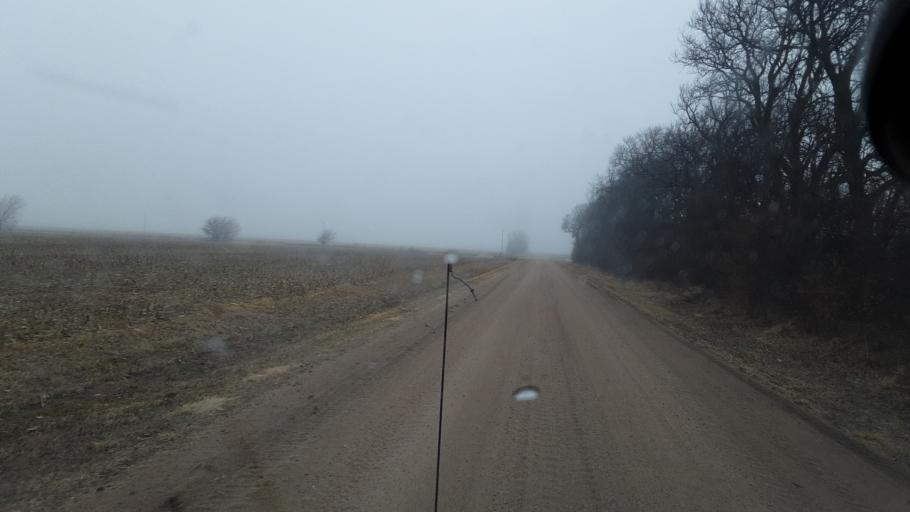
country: US
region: Kansas
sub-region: Reno County
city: South Hutchinson
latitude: 37.9553
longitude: -97.9558
